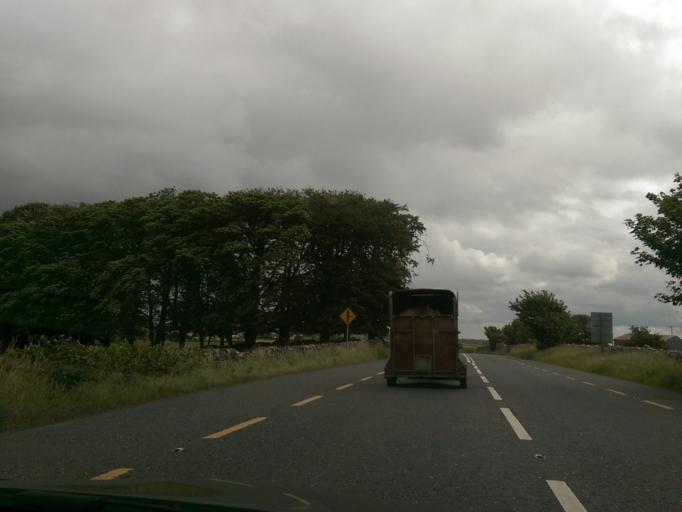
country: IE
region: Connaught
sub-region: County Galway
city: Loughrea
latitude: 53.2052
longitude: -8.5310
